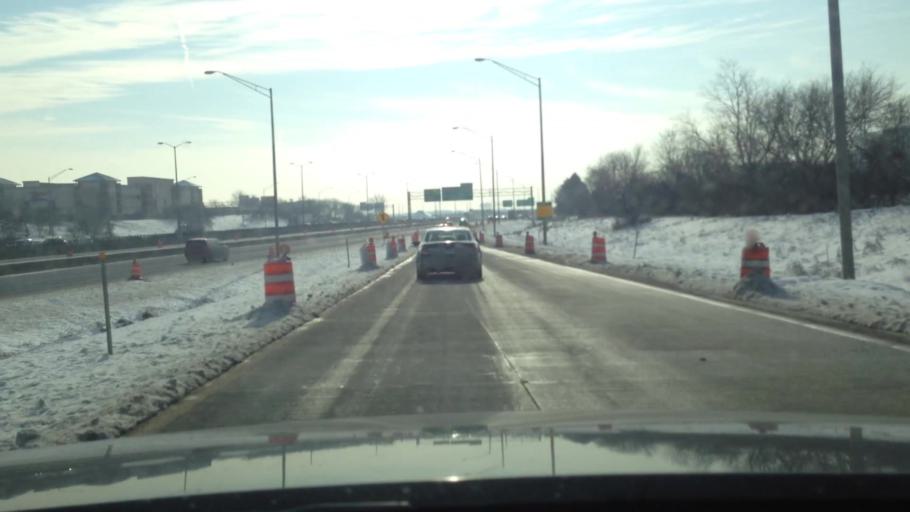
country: US
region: Illinois
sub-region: DuPage County
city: Downers Grove
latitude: 41.8310
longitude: -88.0294
